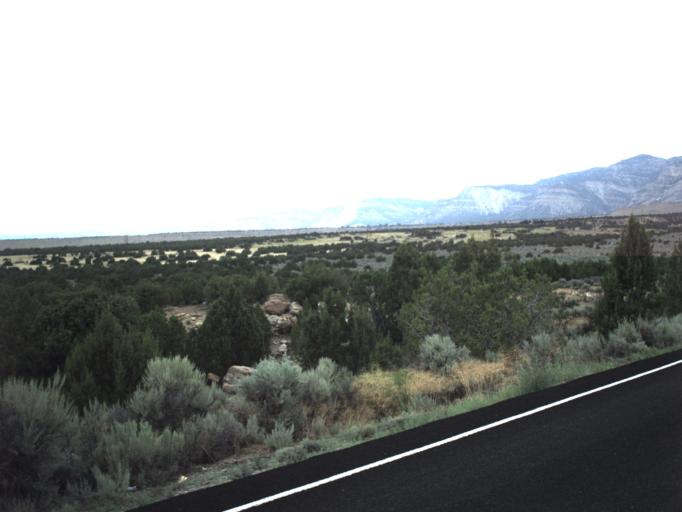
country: US
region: Utah
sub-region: Carbon County
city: East Carbon City
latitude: 39.5058
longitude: -110.3968
